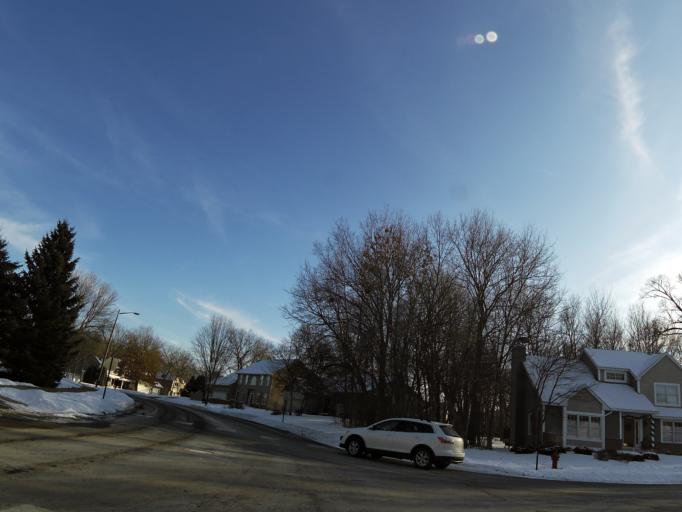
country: US
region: Minnesota
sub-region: Scott County
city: Savage
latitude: 44.7355
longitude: -93.3513
